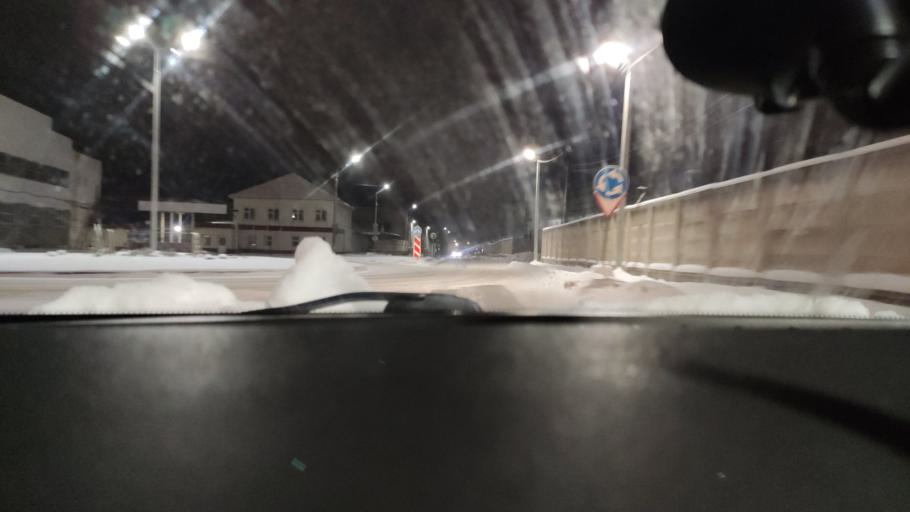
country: RU
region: Perm
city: Krasnokamsk
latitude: 58.0718
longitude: 55.7832
